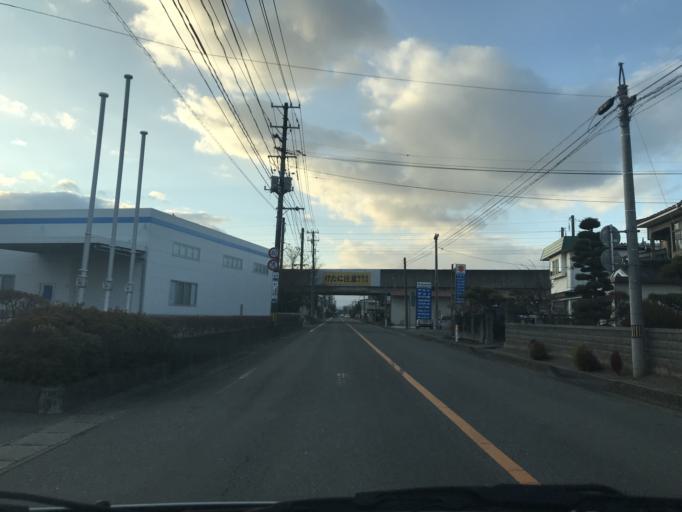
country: JP
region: Miyagi
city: Furukawa
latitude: 38.6580
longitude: 141.0214
